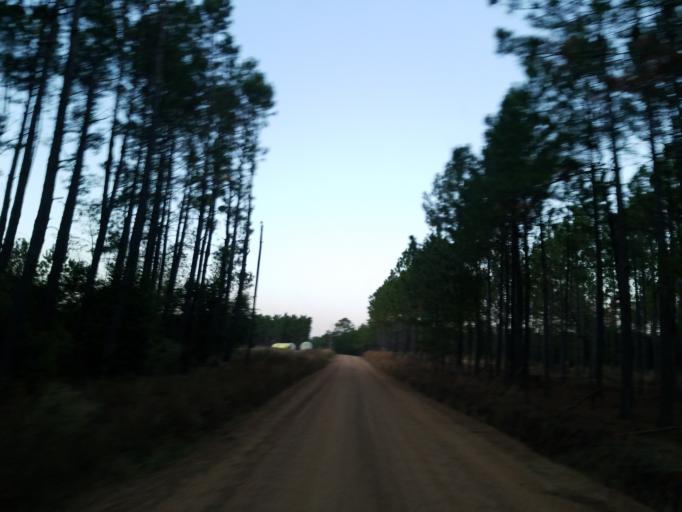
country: US
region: Georgia
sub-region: Turner County
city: Ashburn
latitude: 31.7371
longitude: -83.4846
